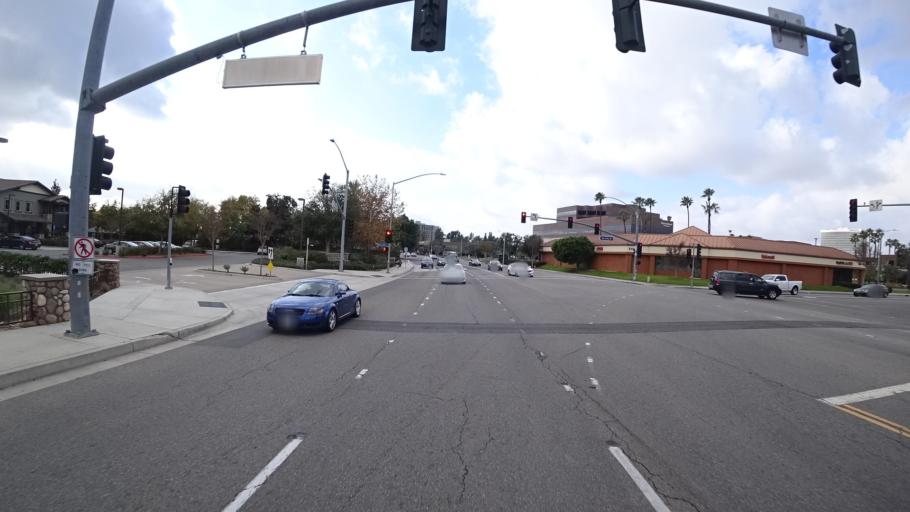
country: US
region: California
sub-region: Orange County
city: Santa Ana
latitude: 33.7743
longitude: -117.8906
